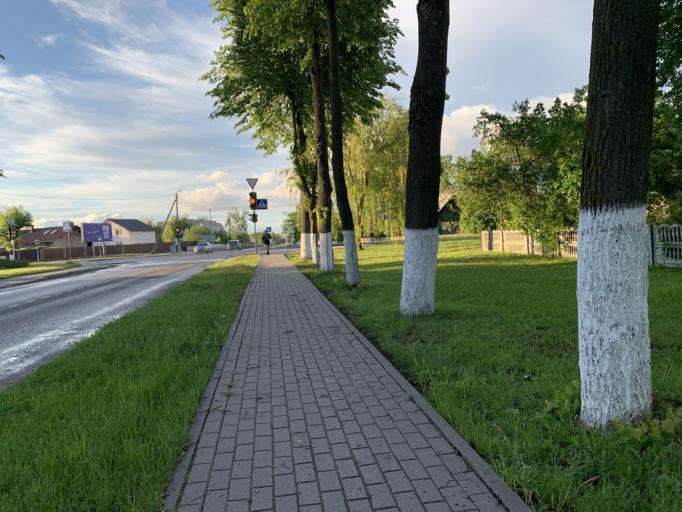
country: BY
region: Minsk
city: Nyasvizh
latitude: 53.2123
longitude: 26.6978
